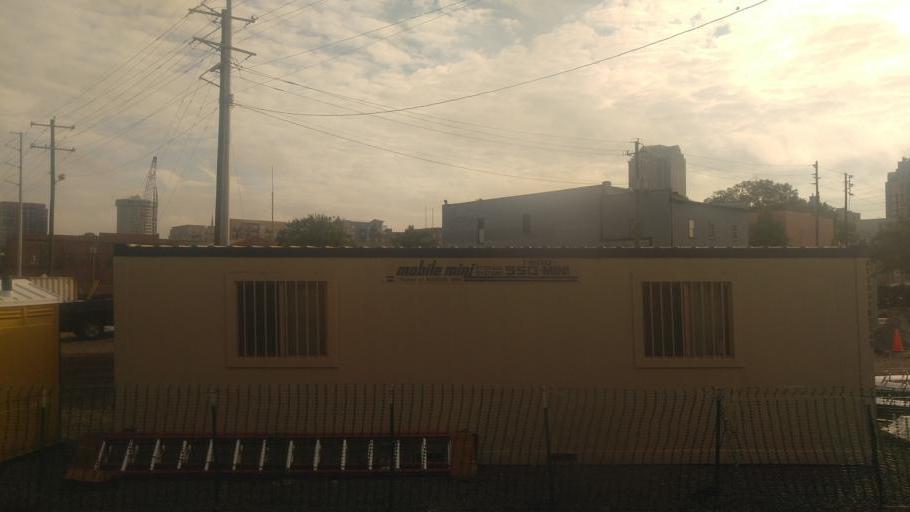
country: US
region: North Carolina
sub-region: Wake County
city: Raleigh
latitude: 35.7753
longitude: -78.6461
